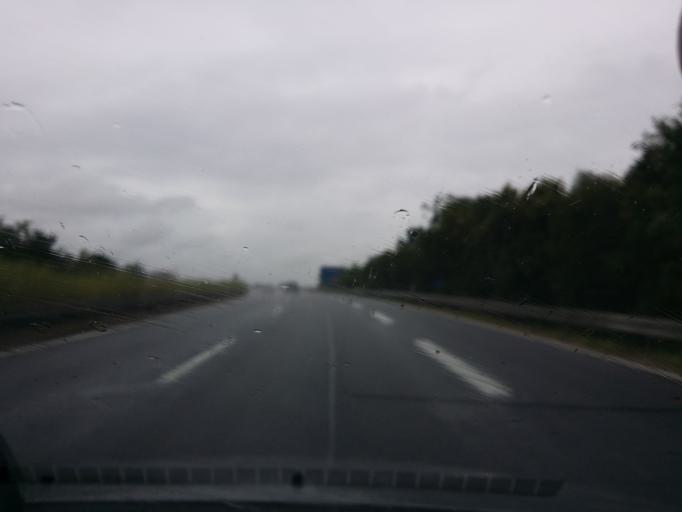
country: DE
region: Hesse
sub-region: Regierungsbezirk Darmstadt
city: Hochheim am Main
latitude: 49.9940
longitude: 8.3441
